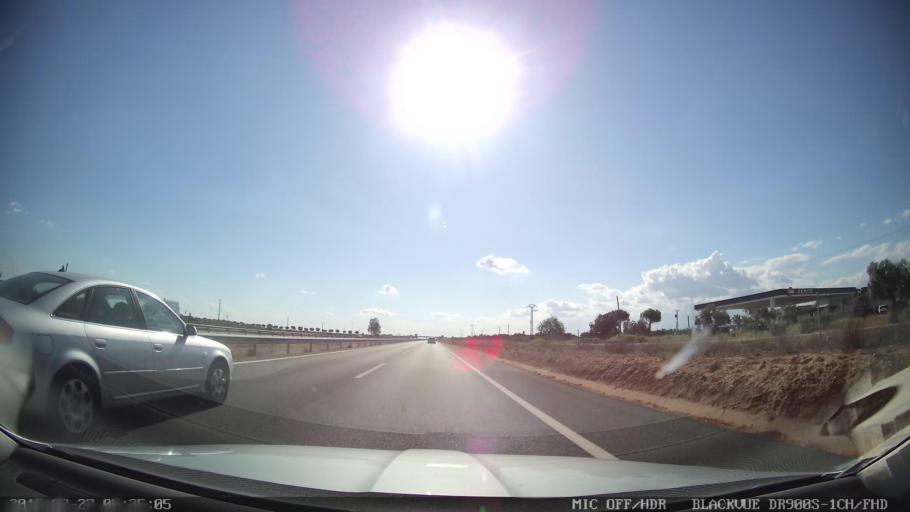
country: ES
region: Castille-La Mancha
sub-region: Province of Toledo
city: Illan de Vacas
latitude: 40.0162
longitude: -4.5605
